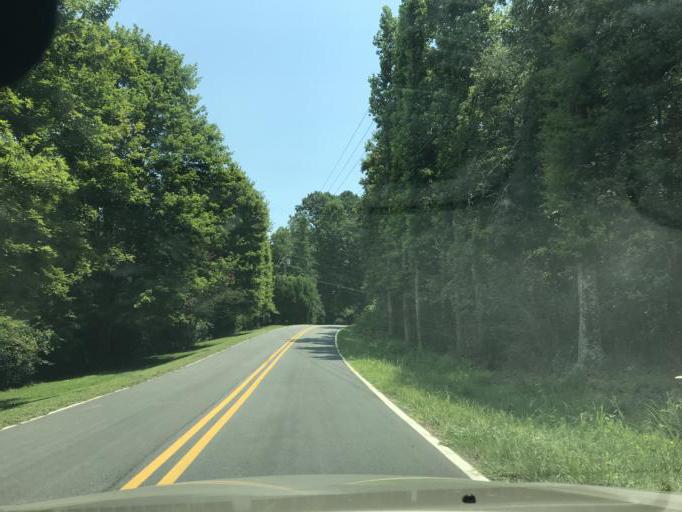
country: US
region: Georgia
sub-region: Forsyth County
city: Cumming
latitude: 34.3125
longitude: -84.1995
